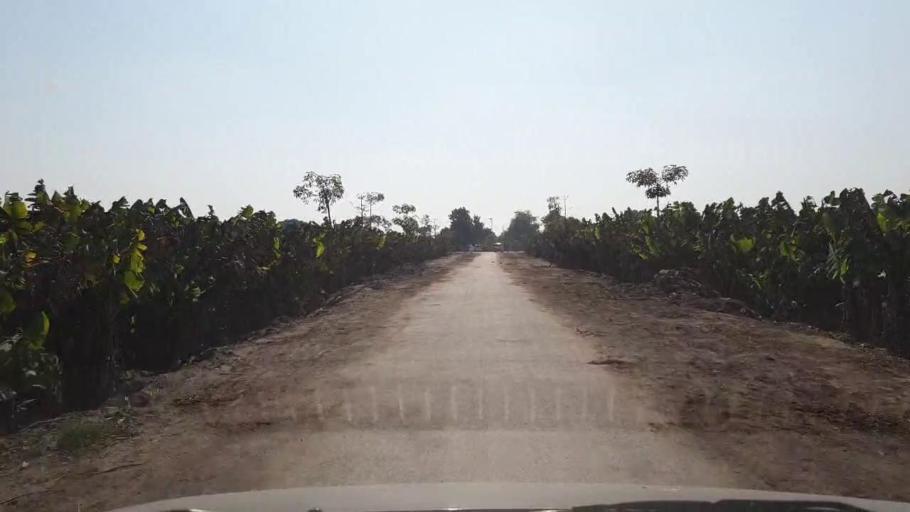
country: PK
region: Sindh
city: Tando Jam
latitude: 25.4159
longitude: 68.6321
